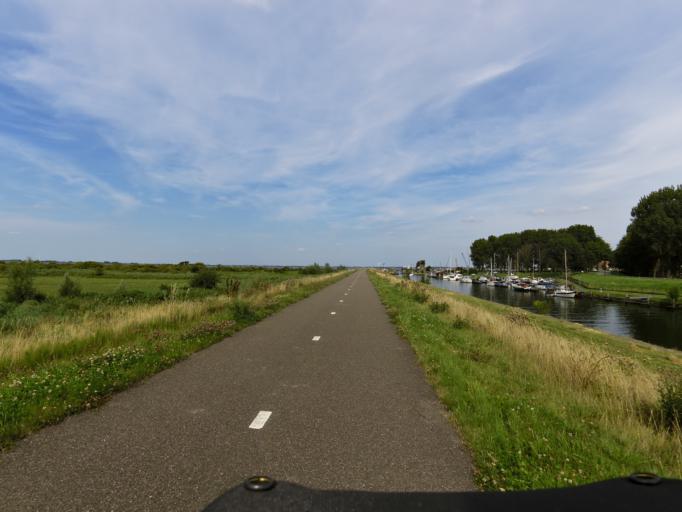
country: NL
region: South Holland
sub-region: Gemeente Goeree-Overflakkee
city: Middelharnis
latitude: 51.7717
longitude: 4.1857
